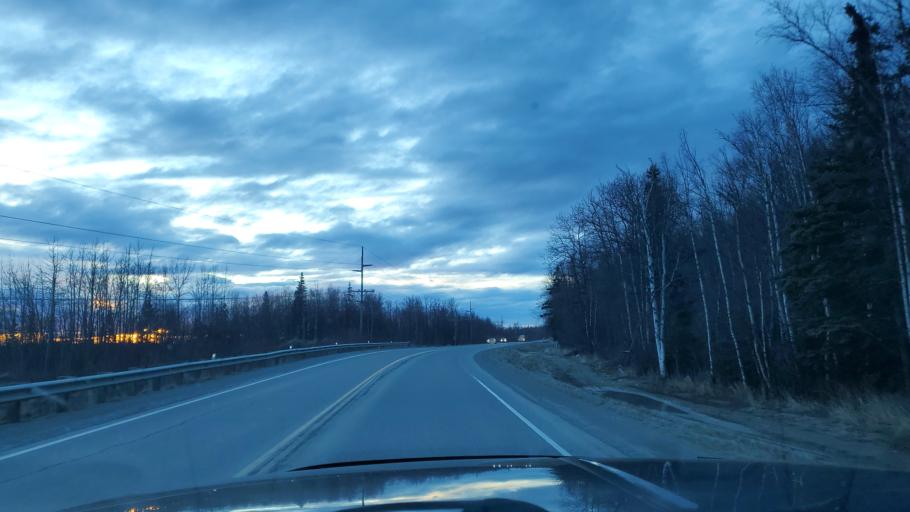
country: US
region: Alaska
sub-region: Matanuska-Susitna Borough
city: Lakes
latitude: 61.6081
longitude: -149.3347
